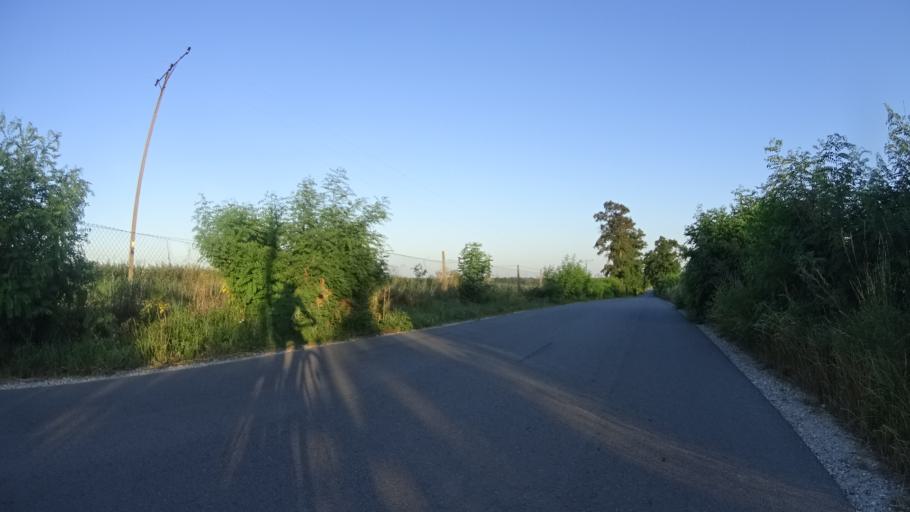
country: PL
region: Masovian Voivodeship
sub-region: Powiat grojecki
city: Goszczyn
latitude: 51.6879
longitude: 20.8199
